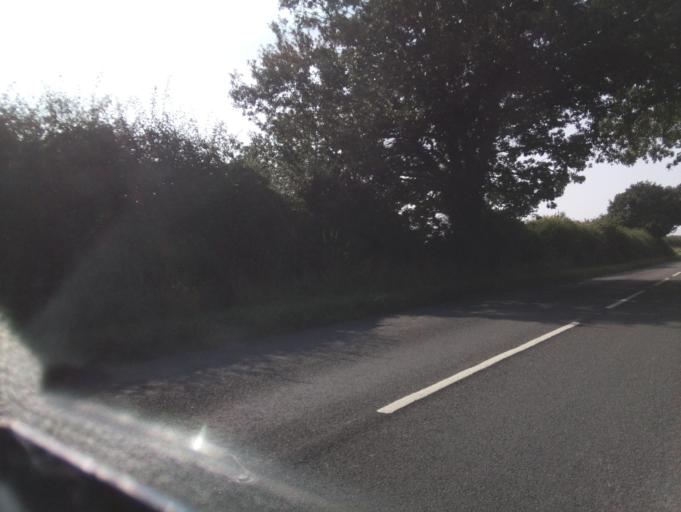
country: GB
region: England
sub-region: Staffordshire
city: Shenstone
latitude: 52.6626
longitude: -1.8742
